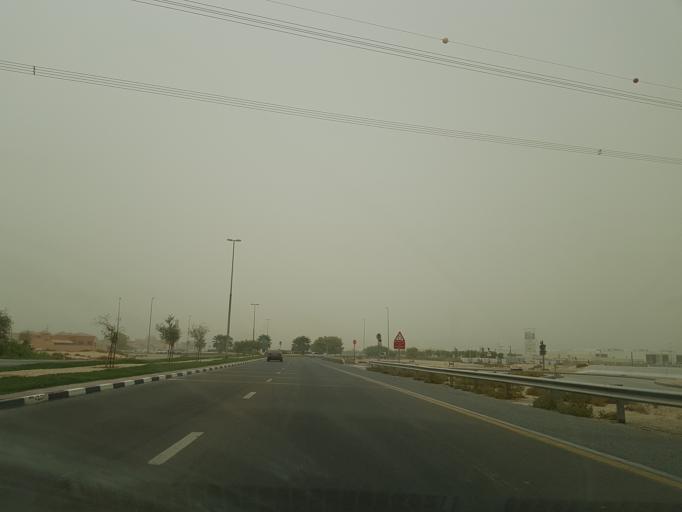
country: AE
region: Dubai
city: Dubai
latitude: 25.1568
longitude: 55.2784
